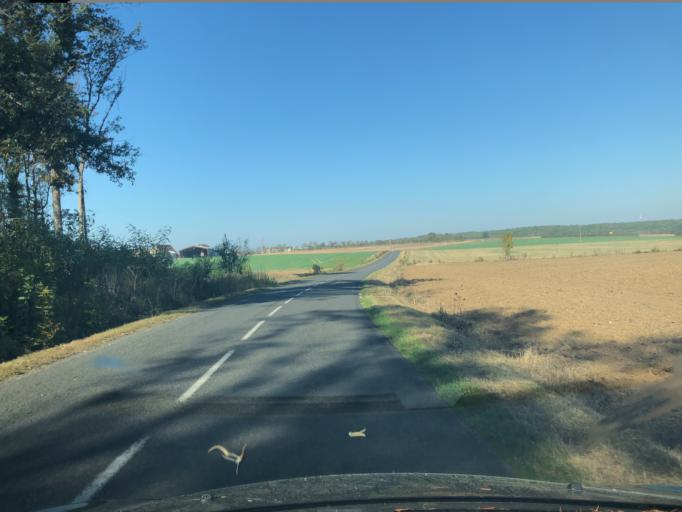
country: FR
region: Centre
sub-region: Departement d'Indre-et-Loire
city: Neuvy-le-Roi
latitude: 47.5734
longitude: 0.5992
